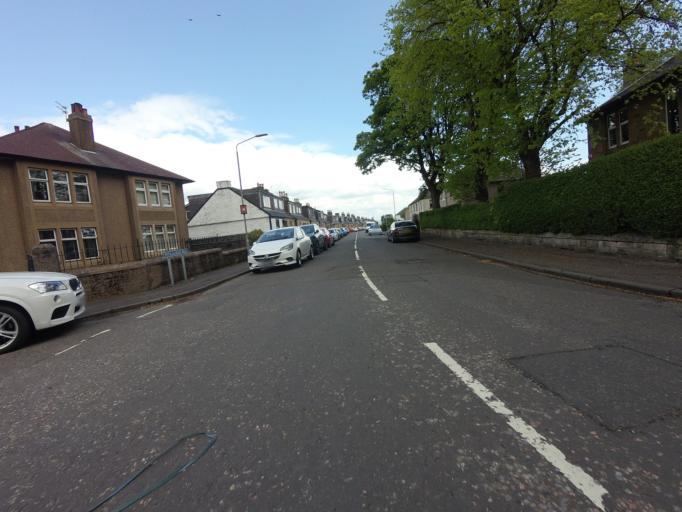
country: GB
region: Scotland
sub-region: Falkirk
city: Falkirk
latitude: 56.0105
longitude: -3.7956
